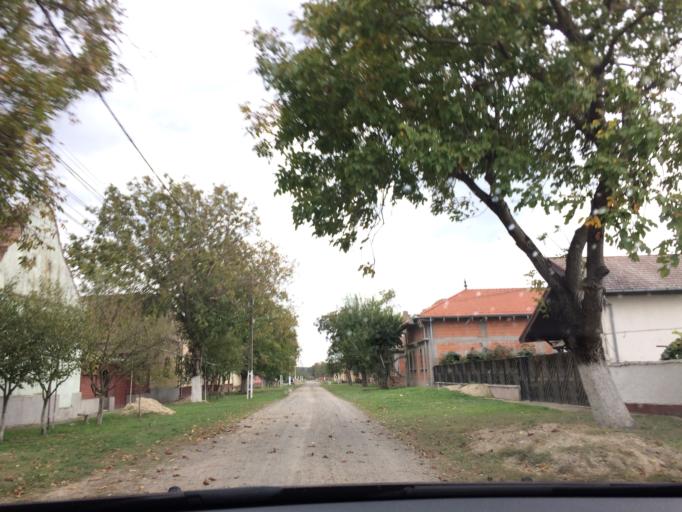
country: RO
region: Timis
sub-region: Comuna Cheveresu Mare
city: Cheveresu Mare
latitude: 45.7319
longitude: 21.4905
